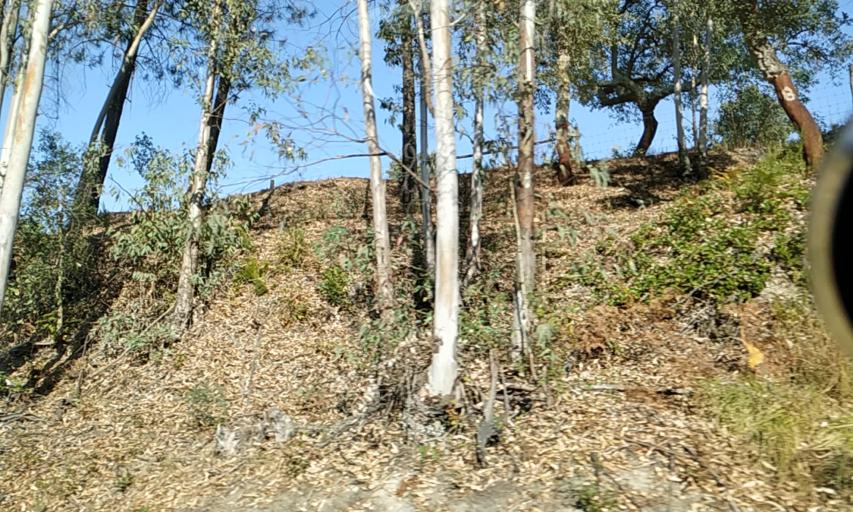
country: PT
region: Santarem
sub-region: Coruche
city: Coruche
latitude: 39.0601
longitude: -8.5663
